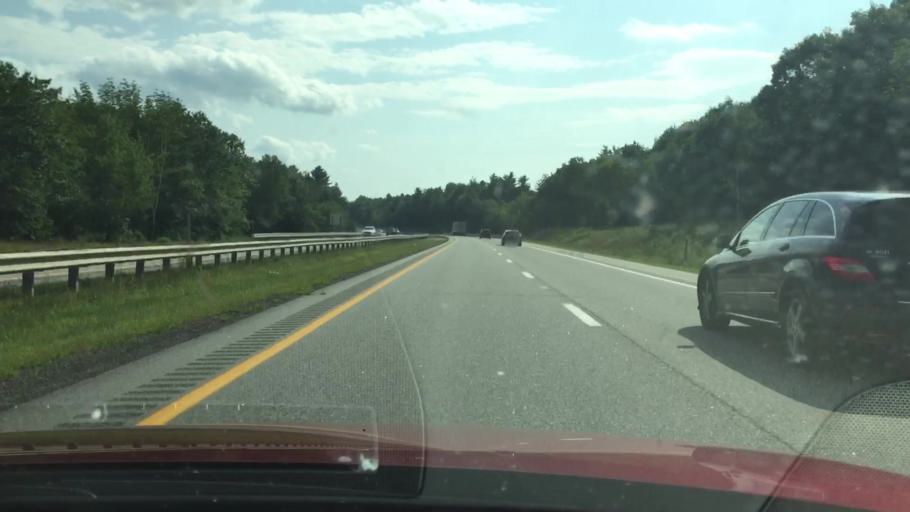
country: US
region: Maine
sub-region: Cumberland County
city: New Gloucester
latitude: 44.0091
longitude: -70.3029
